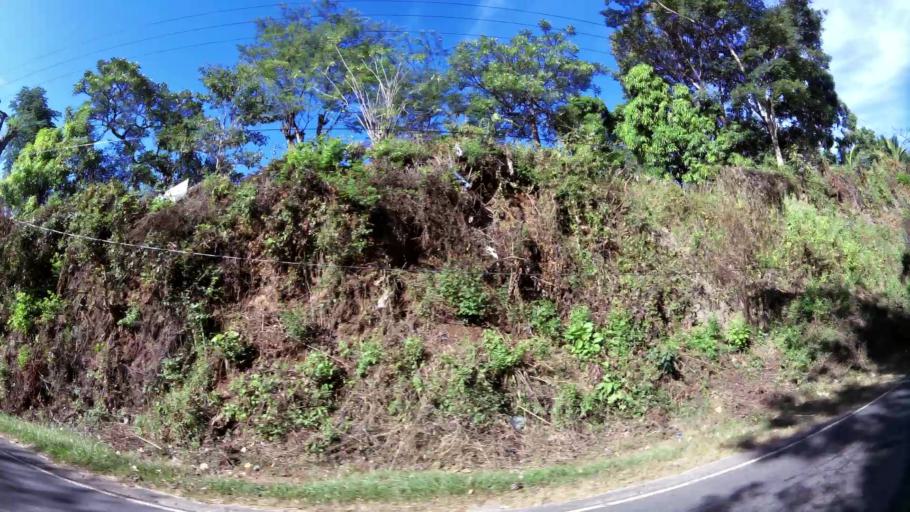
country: SV
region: Cuscatlan
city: Tenancingo
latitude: 13.8435
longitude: -89.0297
